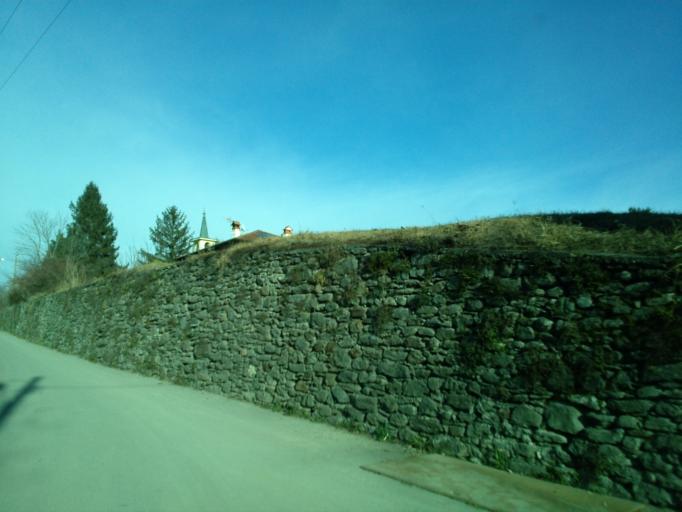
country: IT
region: Lombardy
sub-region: Provincia di Lecco
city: Colico Piano
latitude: 46.1230
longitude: 9.3575
